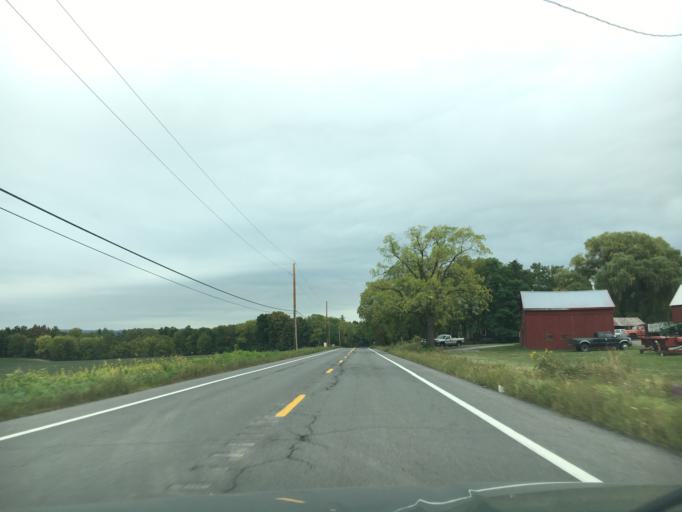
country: US
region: New York
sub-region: Tompkins County
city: Trumansburg
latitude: 42.6707
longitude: -76.7348
